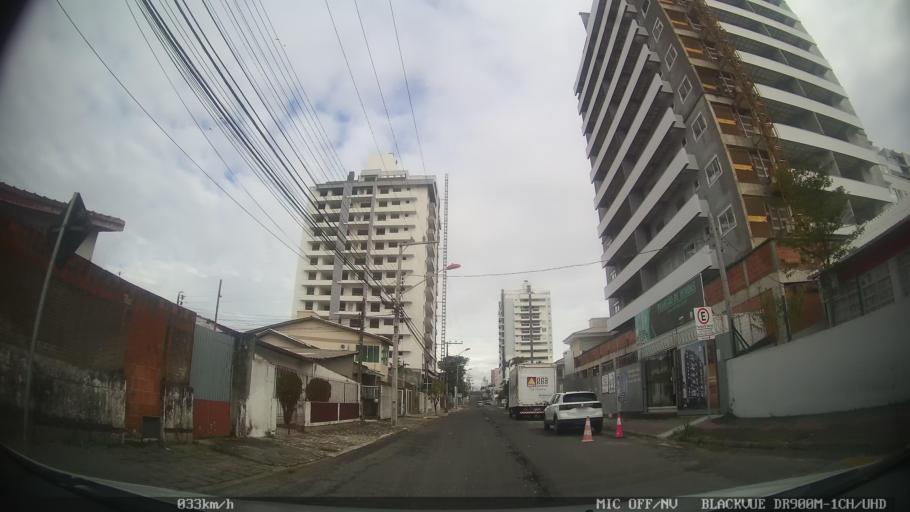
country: BR
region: Santa Catarina
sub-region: Sao Jose
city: Campinas
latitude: -27.5750
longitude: -48.6020
